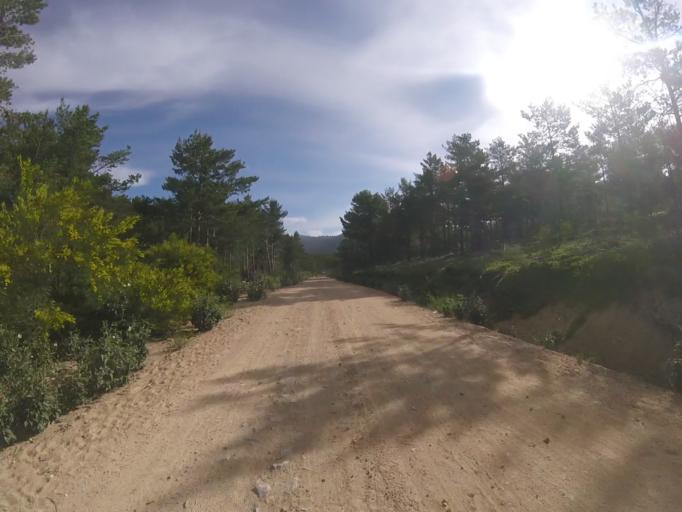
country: ES
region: Castille and Leon
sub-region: Provincia de Avila
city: Peguerinos
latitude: 40.6577
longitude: -4.1854
